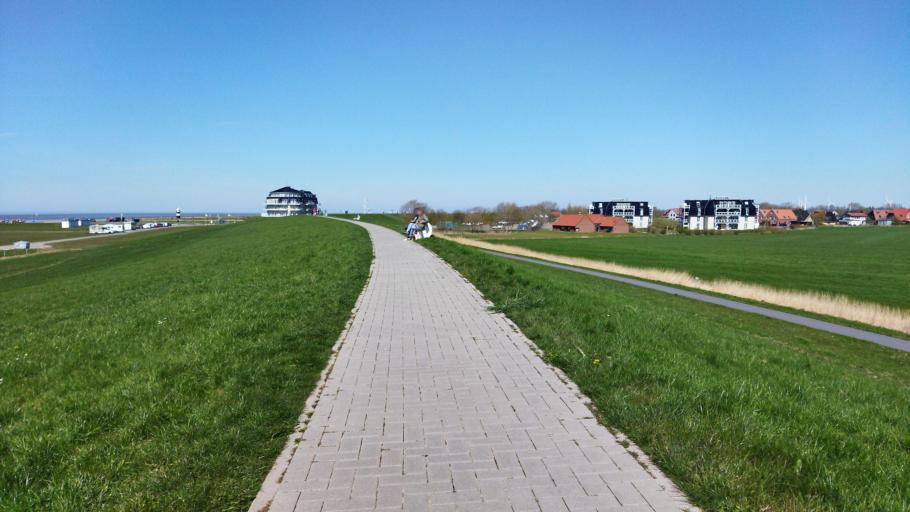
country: DE
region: Lower Saxony
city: Wremen
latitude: 53.6430
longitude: 8.4981
